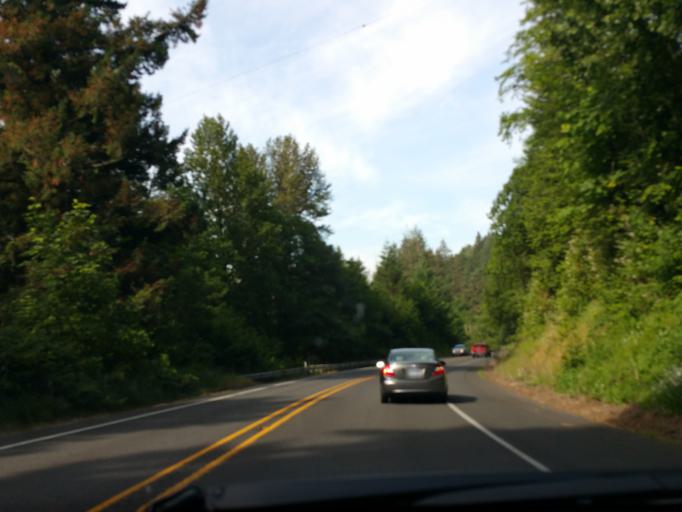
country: US
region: Oregon
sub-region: Hood River County
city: Cascade Locks
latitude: 45.6223
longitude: -122.0264
